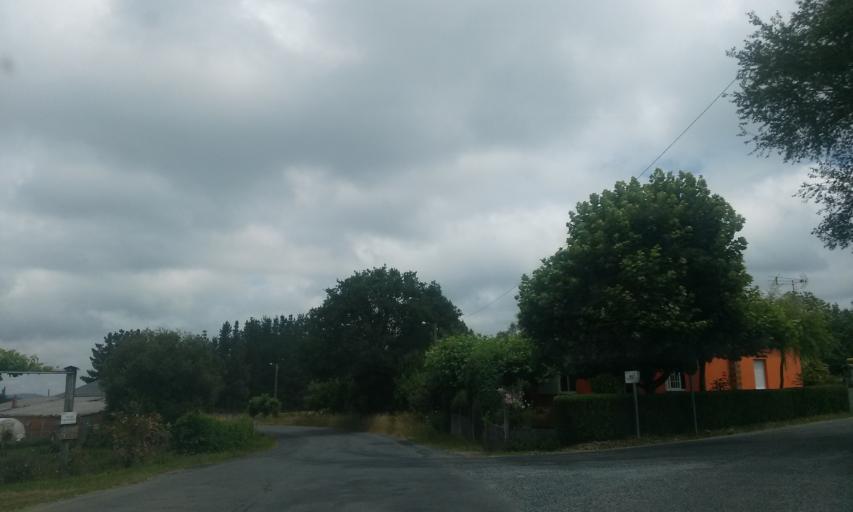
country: ES
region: Galicia
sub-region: Provincia de Lugo
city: Friol
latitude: 43.0868
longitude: -7.8103
